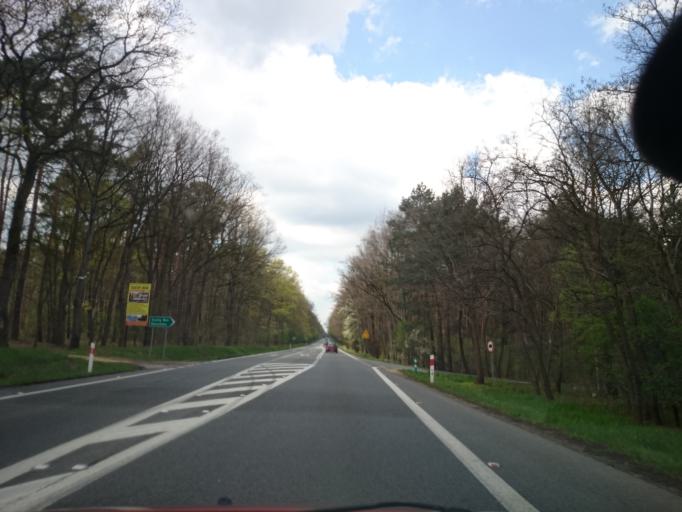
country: PL
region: Opole Voivodeship
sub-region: Powiat opolski
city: Chrzastowice
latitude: 50.6251
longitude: 18.0440
